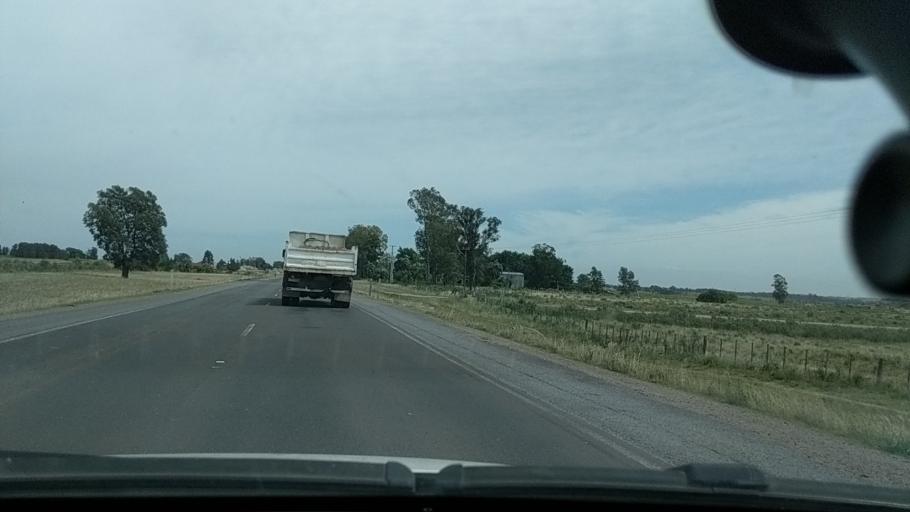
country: UY
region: Durazno
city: Durazno
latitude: -33.4292
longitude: -56.4964
